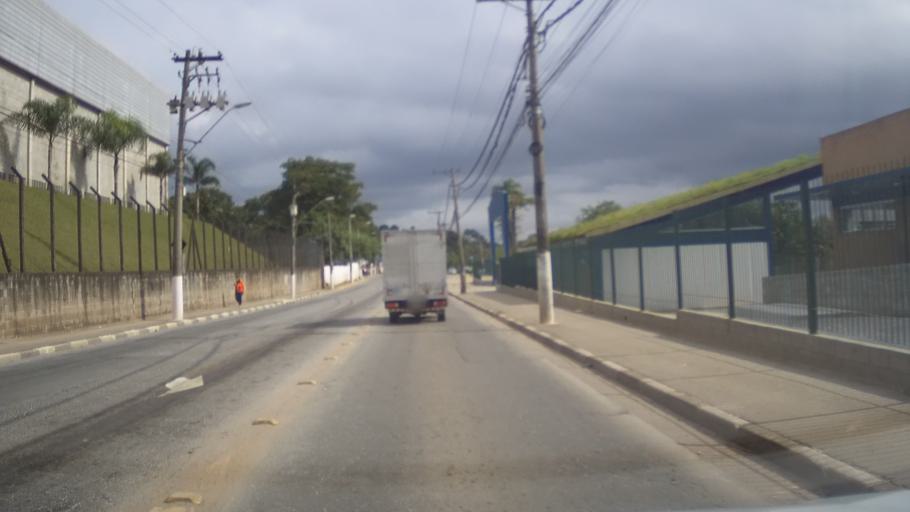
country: BR
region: Sao Paulo
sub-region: Aruja
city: Aruja
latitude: -23.4125
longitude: -46.4088
